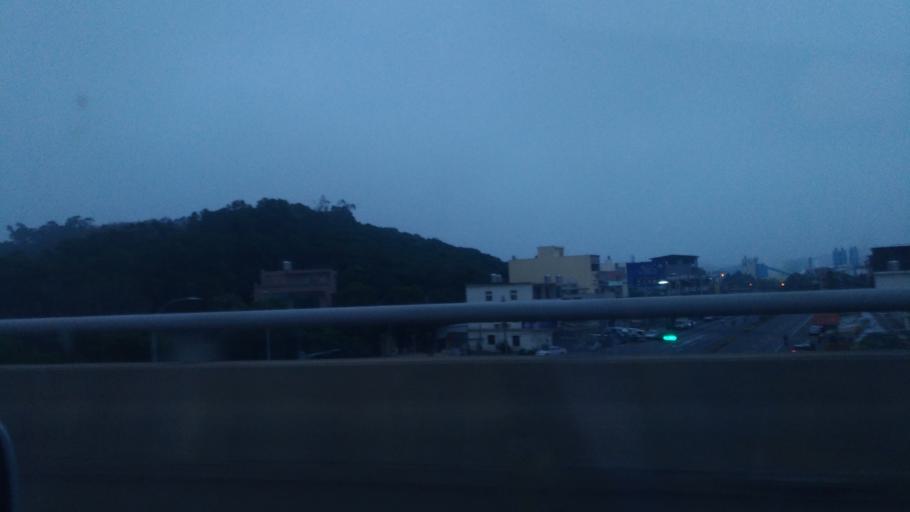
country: TW
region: Taiwan
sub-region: Hsinchu
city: Hsinchu
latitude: 24.7364
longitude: 120.9122
